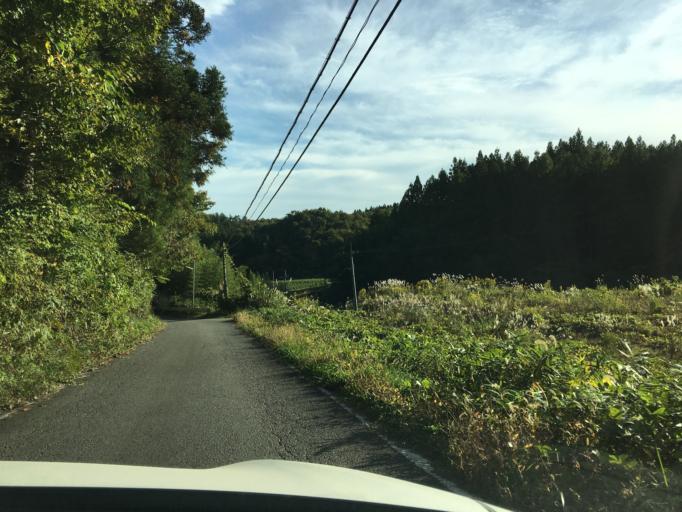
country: JP
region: Fukushima
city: Ishikawa
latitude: 37.2409
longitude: 140.6091
